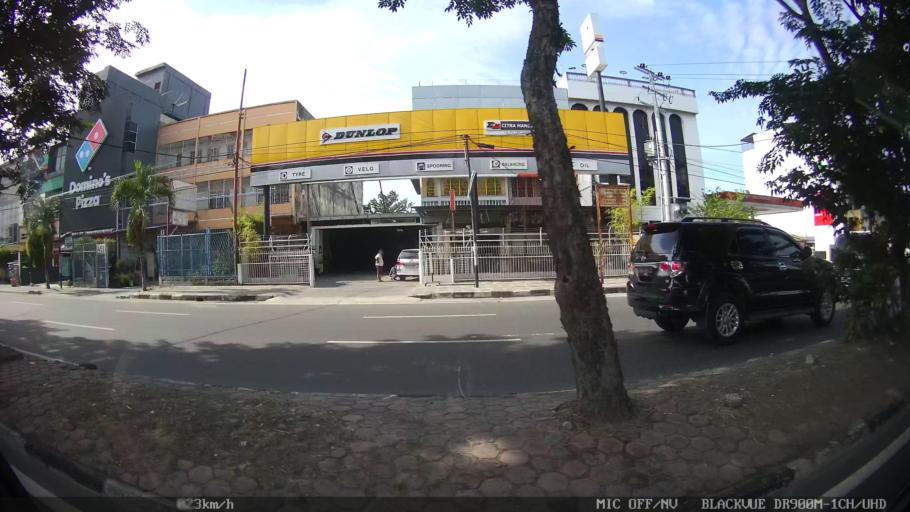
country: ID
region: North Sumatra
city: Medan
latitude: 3.5902
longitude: 98.6565
